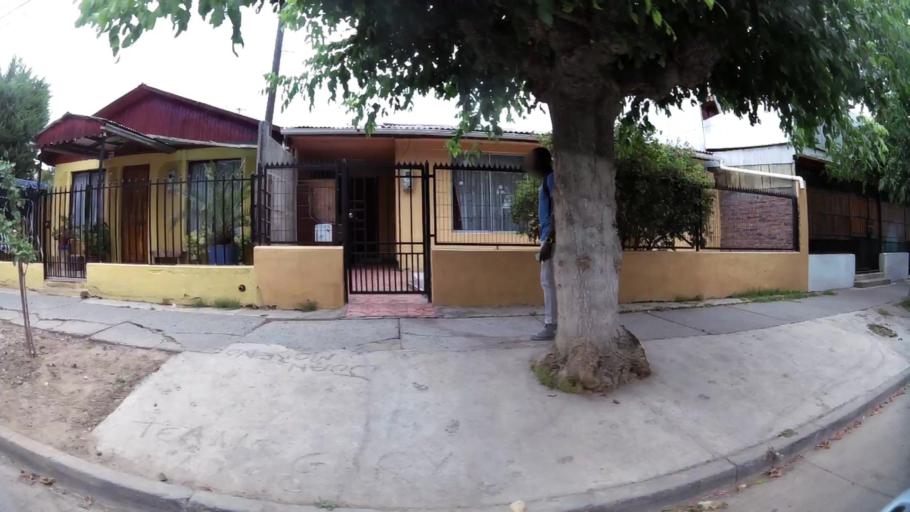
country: CL
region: O'Higgins
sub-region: Provincia de Cachapoal
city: Graneros
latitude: -34.0749
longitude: -70.7249
